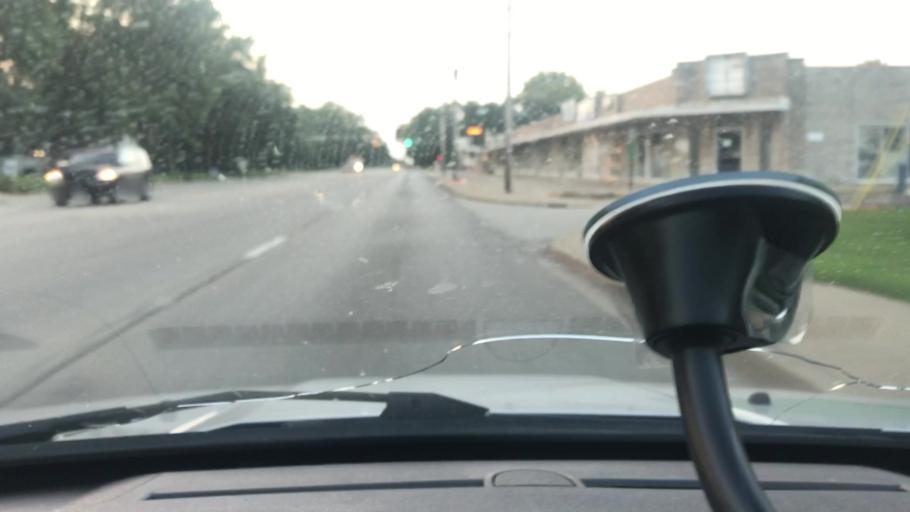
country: US
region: Illinois
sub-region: Tazewell County
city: Pekin
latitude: 40.5807
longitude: -89.6410
